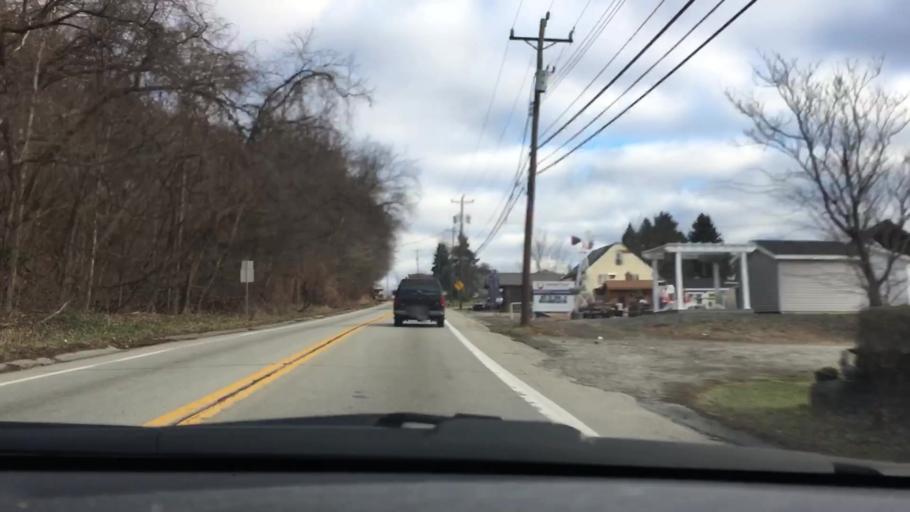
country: US
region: Pennsylvania
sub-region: Westmoreland County
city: Trafford
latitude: 40.3715
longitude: -79.7773
